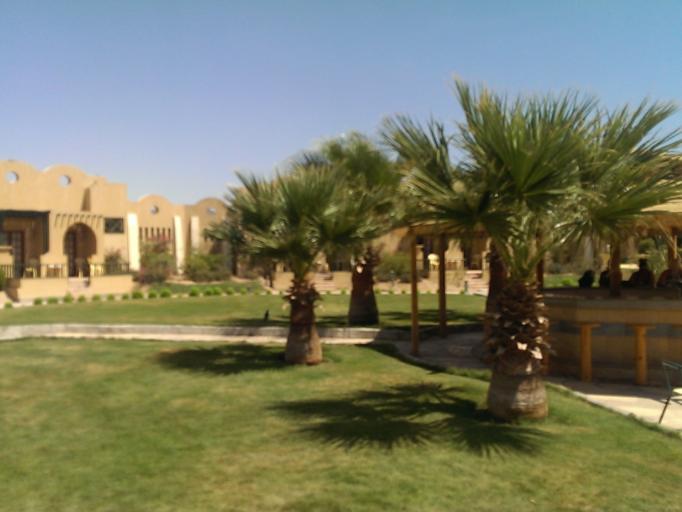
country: EG
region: Red Sea
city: El Gouna
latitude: 27.4000
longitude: 33.6724
